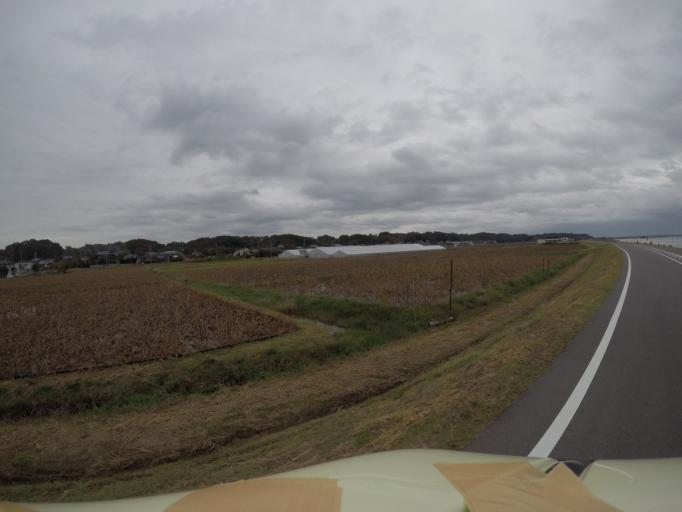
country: JP
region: Ibaraki
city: Inashiki
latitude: 36.0607
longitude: 140.3348
